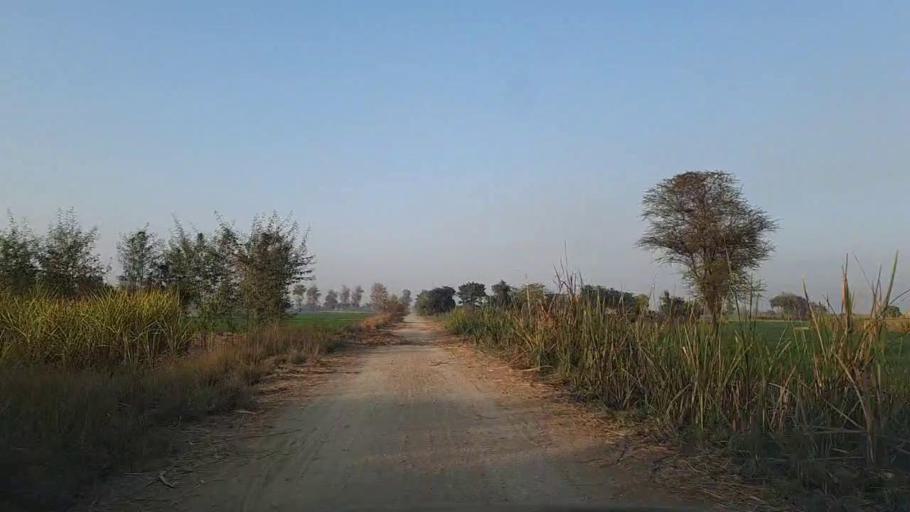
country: PK
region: Sindh
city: Daur
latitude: 26.4828
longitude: 68.4179
